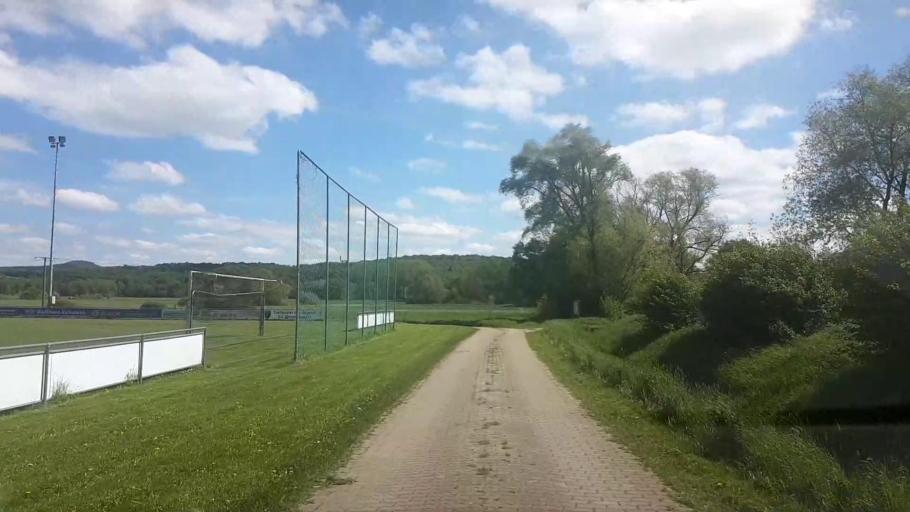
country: DE
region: Bavaria
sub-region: Regierungsbezirk Unterfranken
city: Untermerzbach
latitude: 50.1523
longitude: 10.9046
